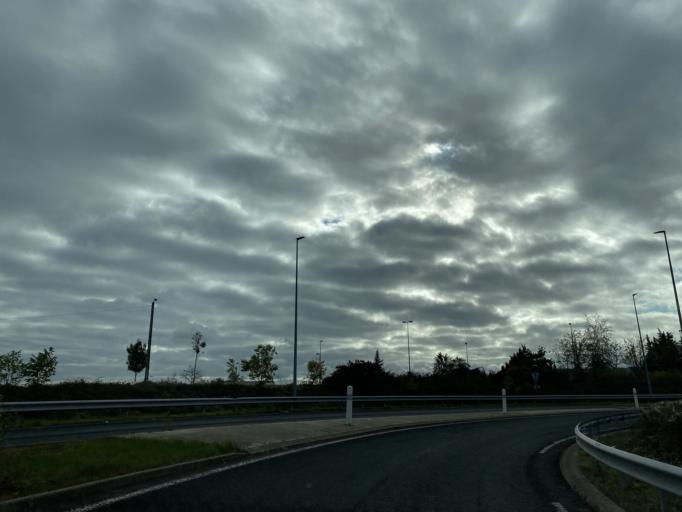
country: FR
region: Auvergne
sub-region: Departement du Puy-de-Dome
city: Aubiere
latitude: 45.7725
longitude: 3.1264
